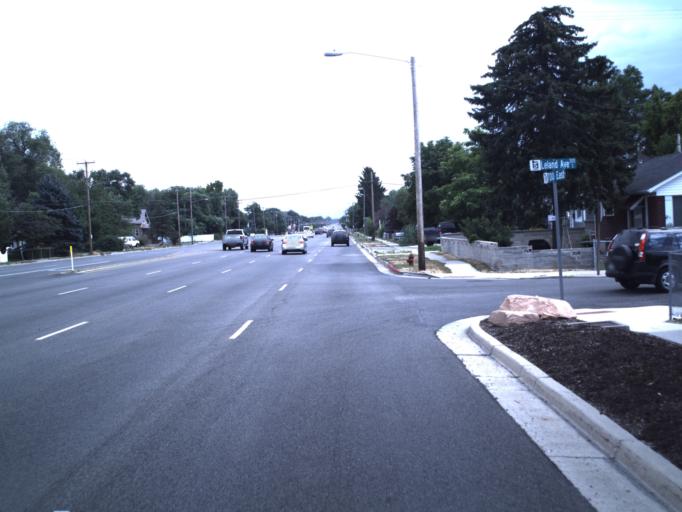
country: US
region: Utah
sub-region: Salt Lake County
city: Millcreek
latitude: 40.7058
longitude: -111.8715
